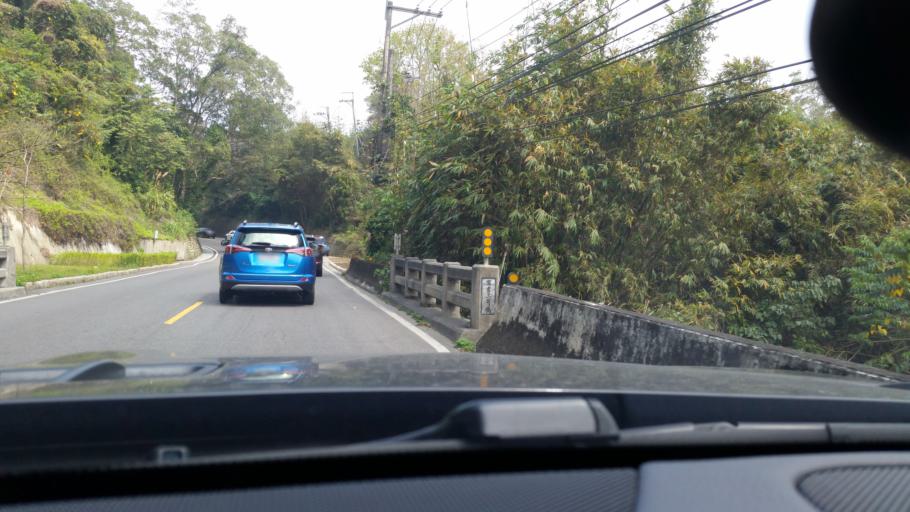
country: TW
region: Taiwan
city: Daxi
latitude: 24.8278
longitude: 121.3148
